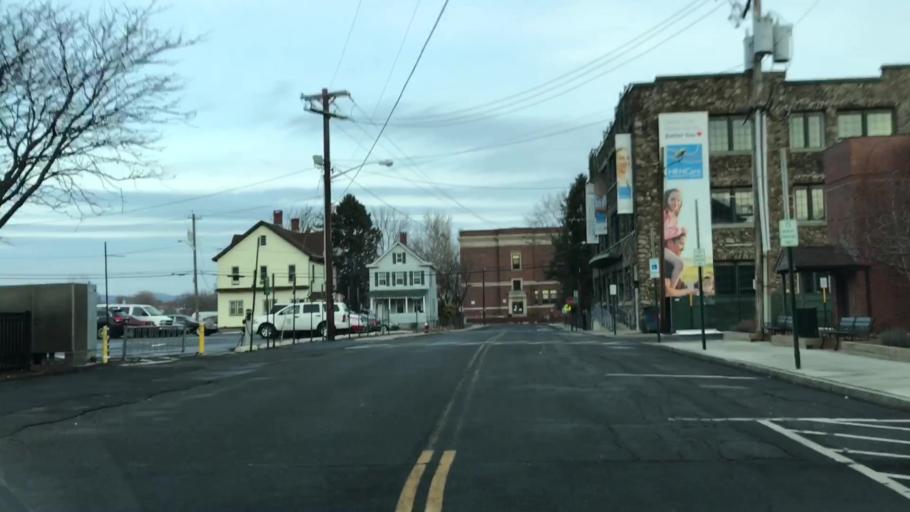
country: US
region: New York
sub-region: Rockland County
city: Haverstraw
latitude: 41.1964
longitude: -73.9664
